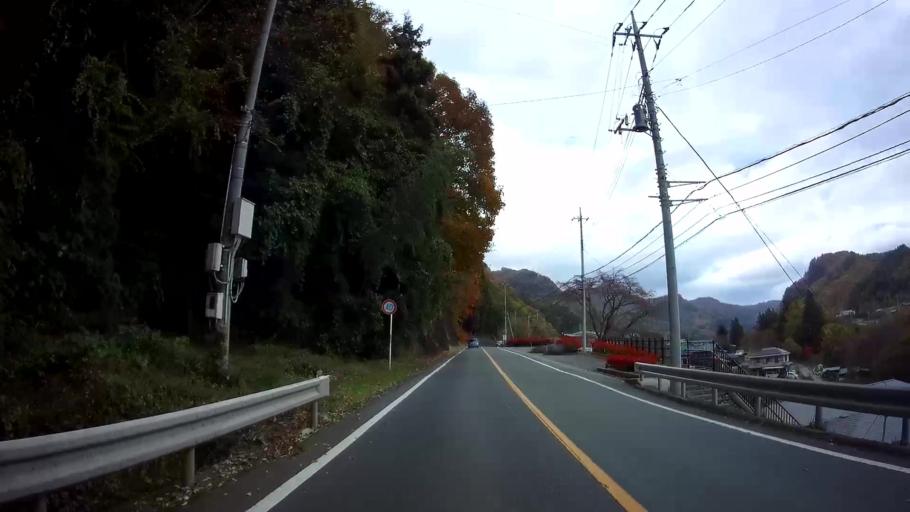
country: JP
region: Gunma
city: Nakanojomachi
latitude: 36.5722
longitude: 138.6251
